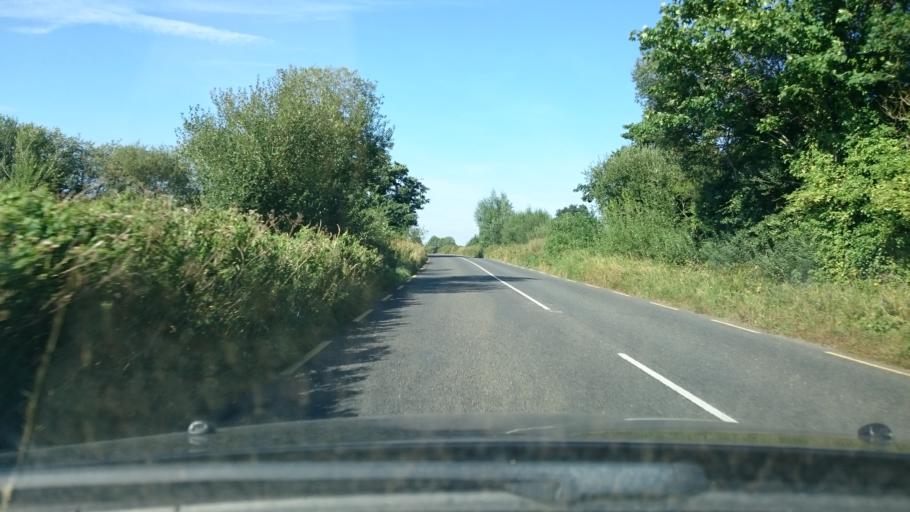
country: IE
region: Leinster
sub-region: Kilkenny
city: Graiguenamanagh
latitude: 52.5606
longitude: -6.9528
